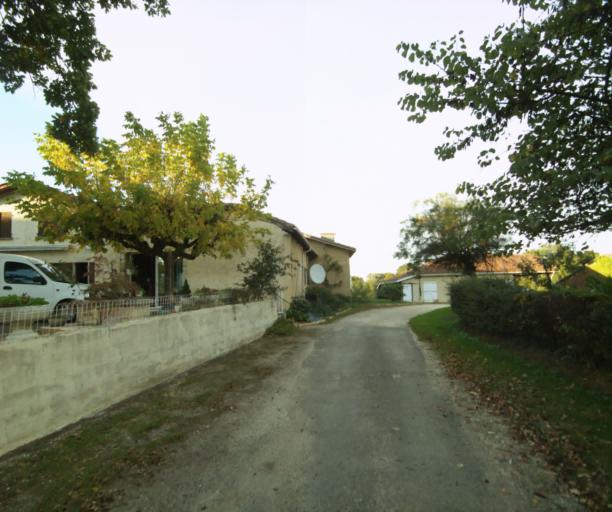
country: FR
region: Midi-Pyrenees
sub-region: Departement du Gers
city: Eauze
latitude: 43.8779
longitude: 0.0454
